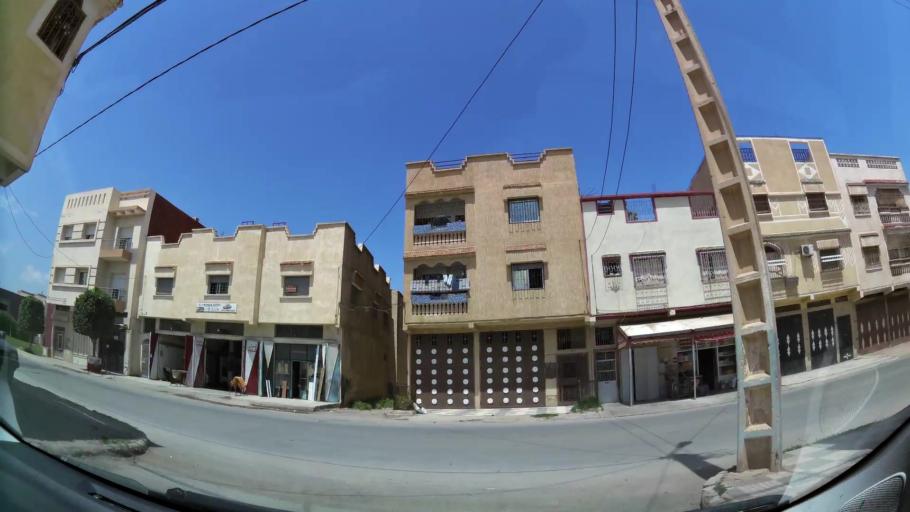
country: MA
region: Oriental
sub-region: Oujda-Angad
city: Oujda
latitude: 34.6884
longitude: -1.8937
